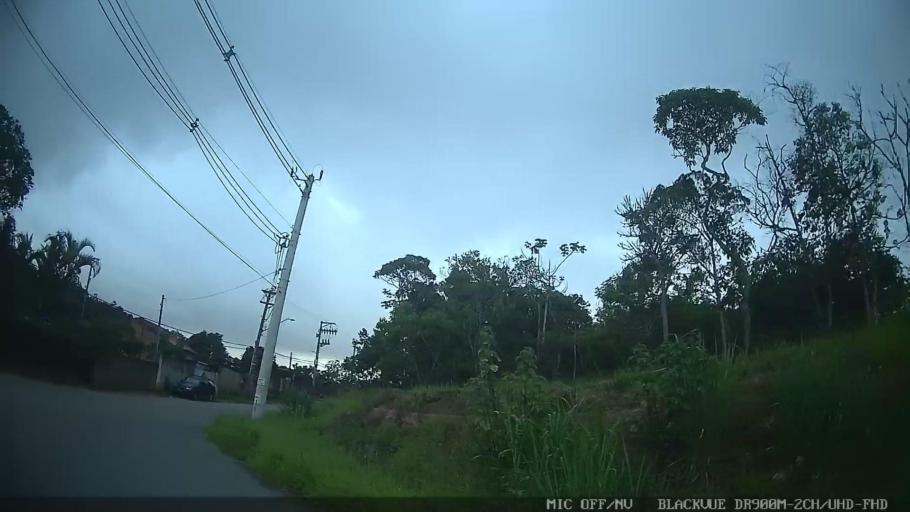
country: BR
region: Sao Paulo
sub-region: Biritiba-Mirim
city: Biritiba Mirim
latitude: -23.5404
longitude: -46.0896
